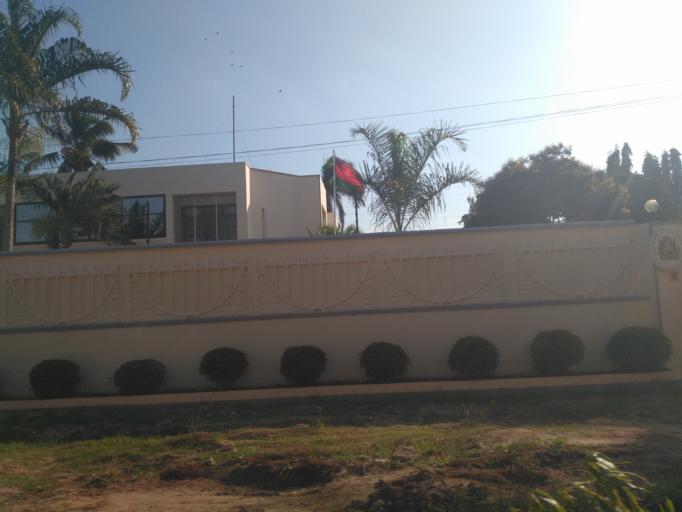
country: TZ
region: Dar es Salaam
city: Magomeni
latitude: -6.7629
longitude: 39.2511
